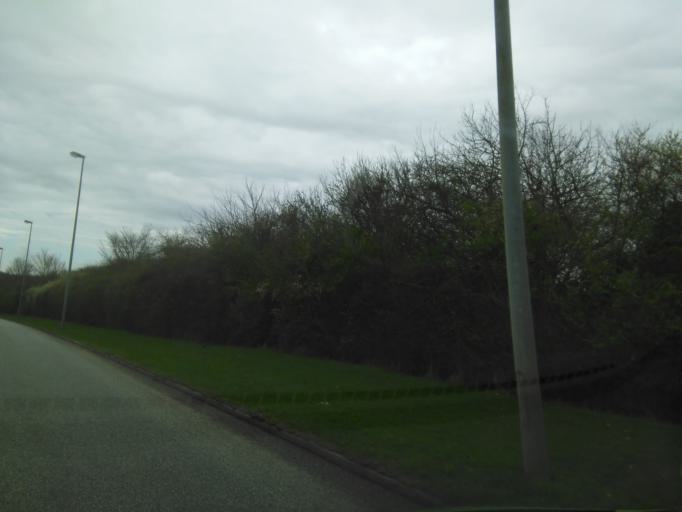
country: DK
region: Central Jutland
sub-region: Arhus Kommune
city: Stavtrup
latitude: 56.1775
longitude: 10.1203
